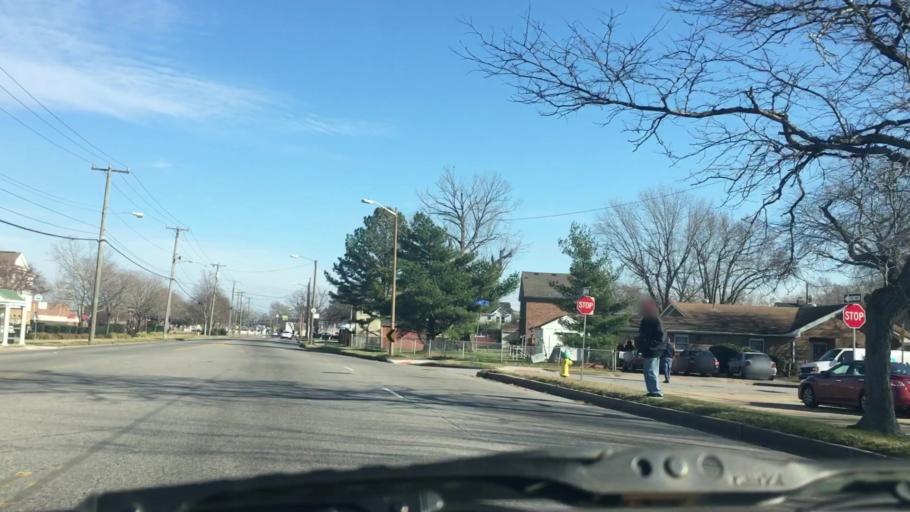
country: US
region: Virginia
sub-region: City of Norfolk
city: Norfolk
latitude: 36.8543
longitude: -76.2618
